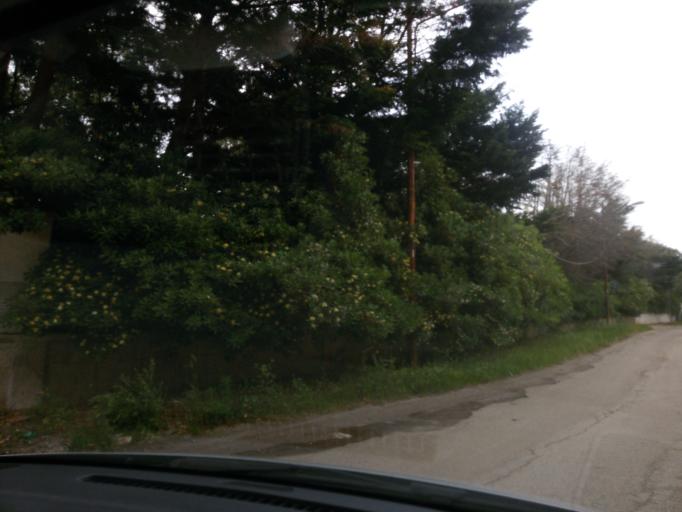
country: IT
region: Apulia
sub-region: Provincia di Brindisi
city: Brindisi
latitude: 40.6570
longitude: 17.9343
